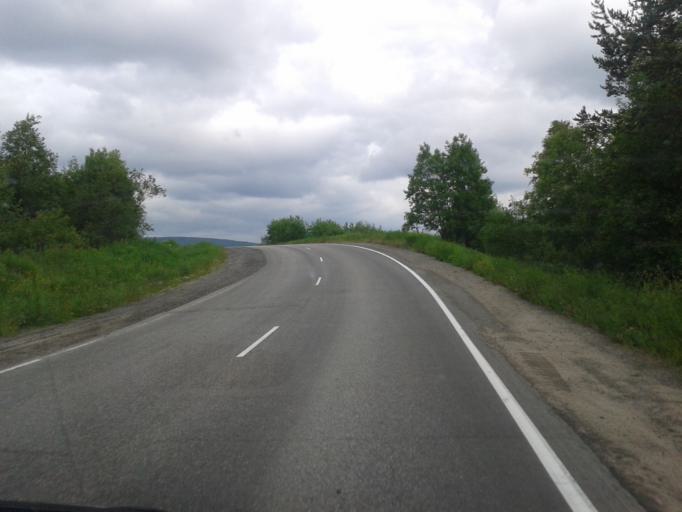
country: RU
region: Murmansk
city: Kandalaksha
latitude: 67.2112
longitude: 32.4423
